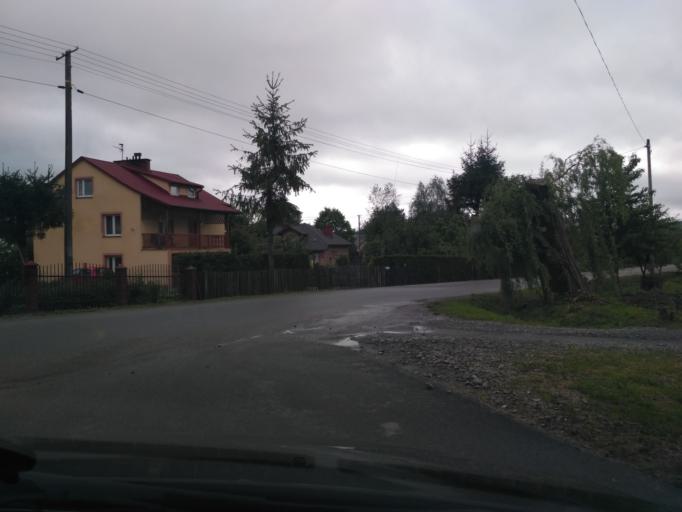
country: PL
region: Subcarpathian Voivodeship
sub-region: Powiat jasielski
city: Kolaczyce
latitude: 49.8006
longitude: 21.4920
